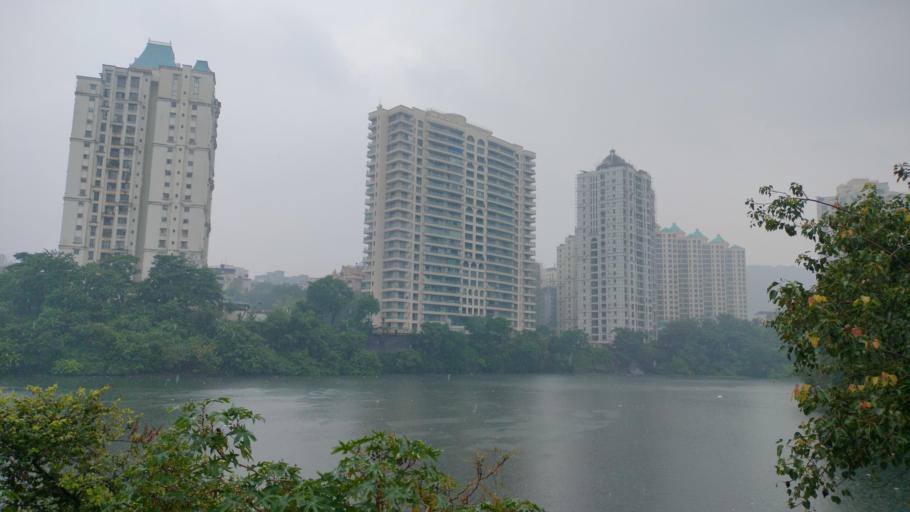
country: IN
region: Maharashtra
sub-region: Mumbai Suburban
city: Powai
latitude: 19.1174
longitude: 72.8992
